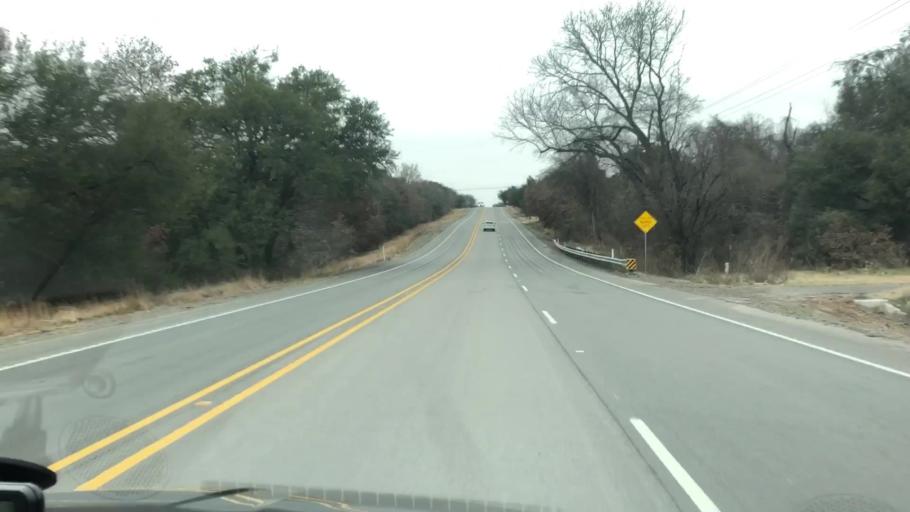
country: US
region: Texas
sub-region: Erath County
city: Stephenville
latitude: 32.1615
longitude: -98.1500
